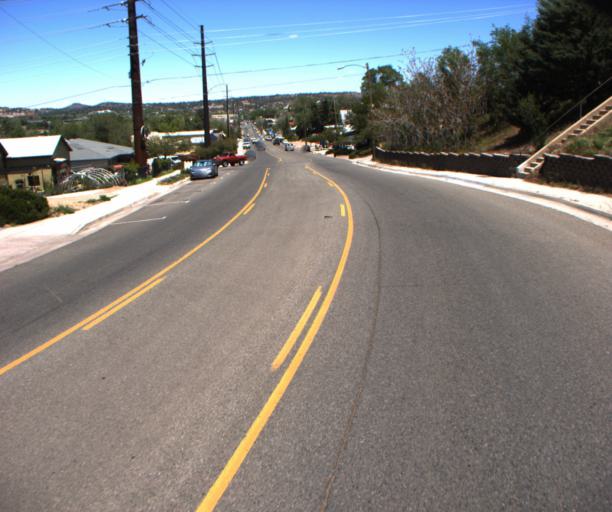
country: US
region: Arizona
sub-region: Yavapai County
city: Prescott
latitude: 34.5316
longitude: -112.4704
